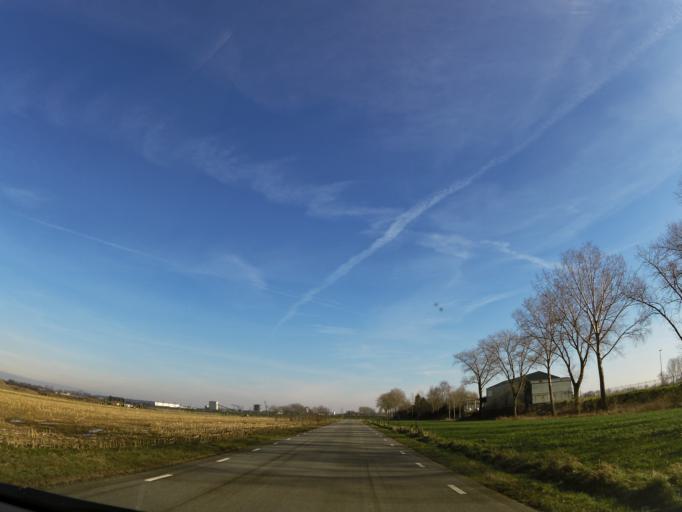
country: NL
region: Limburg
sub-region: Gemeente Sittard-Geleen
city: Born
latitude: 51.0460
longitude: 5.7947
